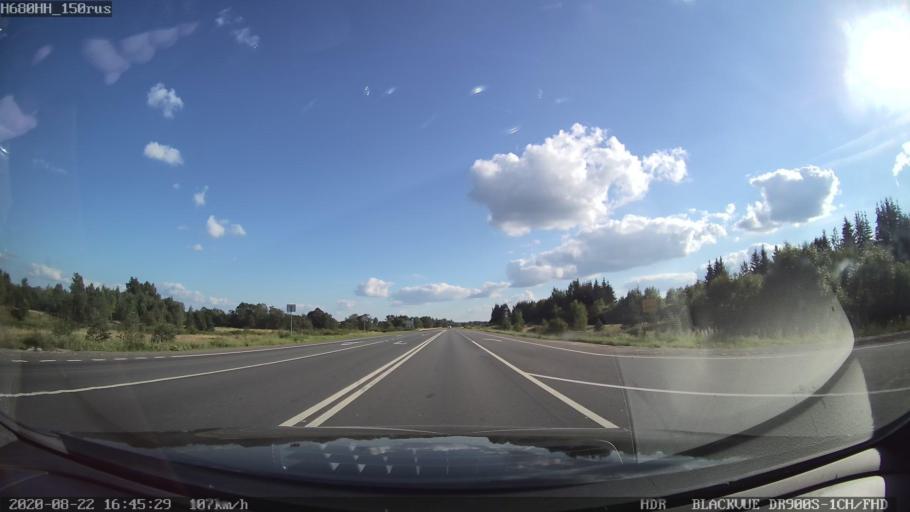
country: RU
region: Tverskaya
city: Rameshki
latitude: 57.2961
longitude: 36.0907
